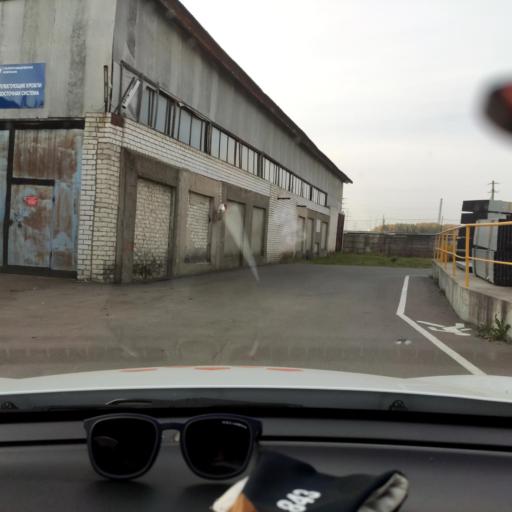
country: RU
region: Tatarstan
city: Staroye Arakchino
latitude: 55.8350
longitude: 49.0292
